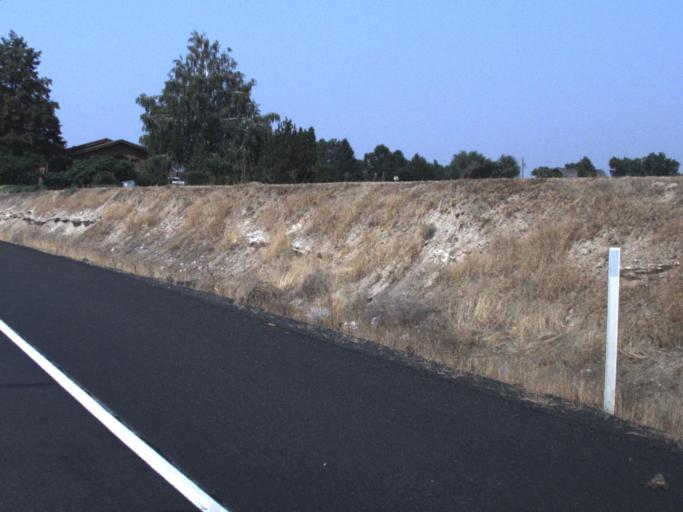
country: US
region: Washington
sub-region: Yakima County
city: Selah
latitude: 46.6792
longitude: -120.5042
